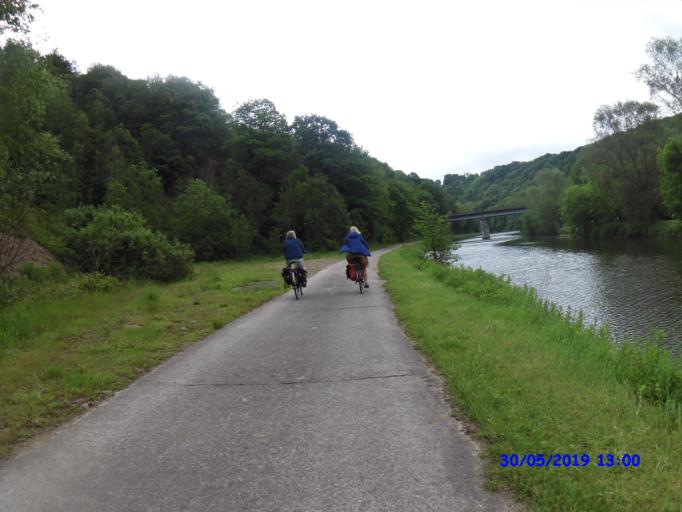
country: BE
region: Wallonia
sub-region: Province du Hainaut
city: Thuin
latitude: 50.3477
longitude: 4.2999
